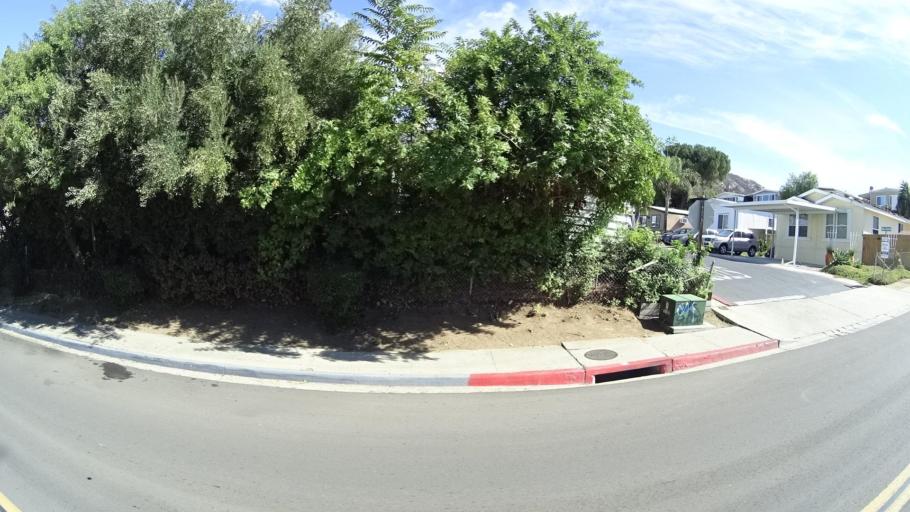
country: US
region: California
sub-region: San Diego County
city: Crest
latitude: 32.8420
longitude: -116.8766
